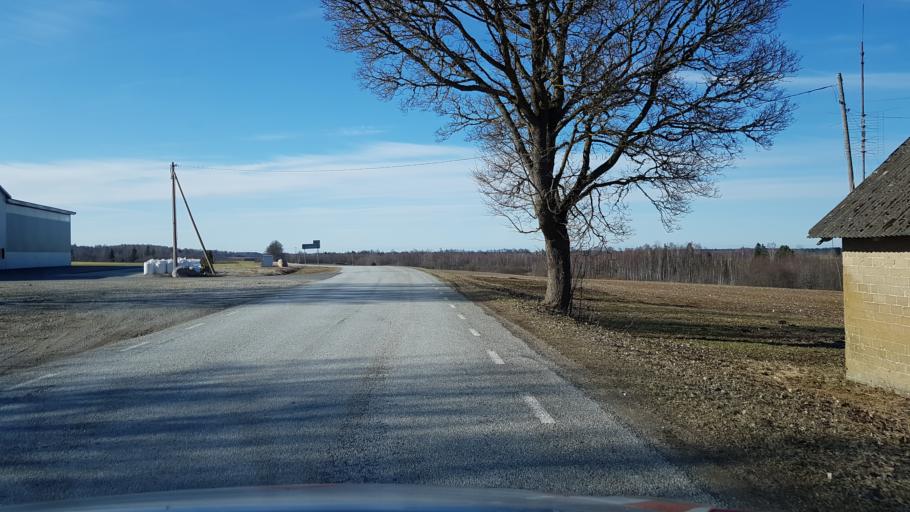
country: EE
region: Laeaene-Virumaa
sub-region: Kadrina vald
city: Kadrina
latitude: 59.2924
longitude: 26.1740
